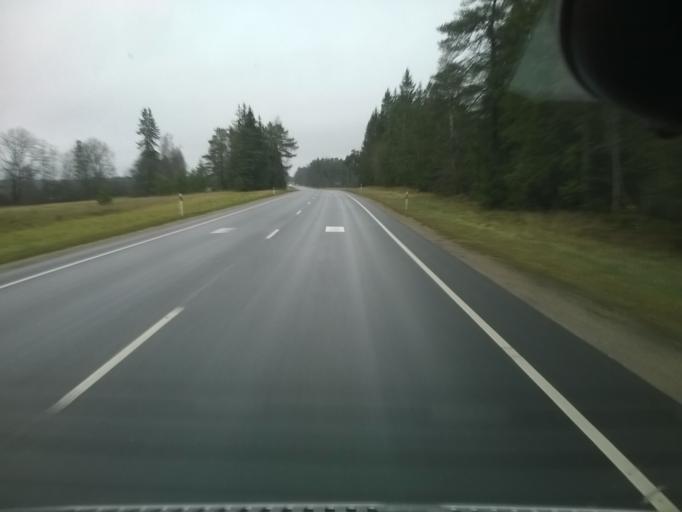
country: EE
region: Harju
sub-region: Nissi vald
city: Turba
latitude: 59.0096
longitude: 24.1307
